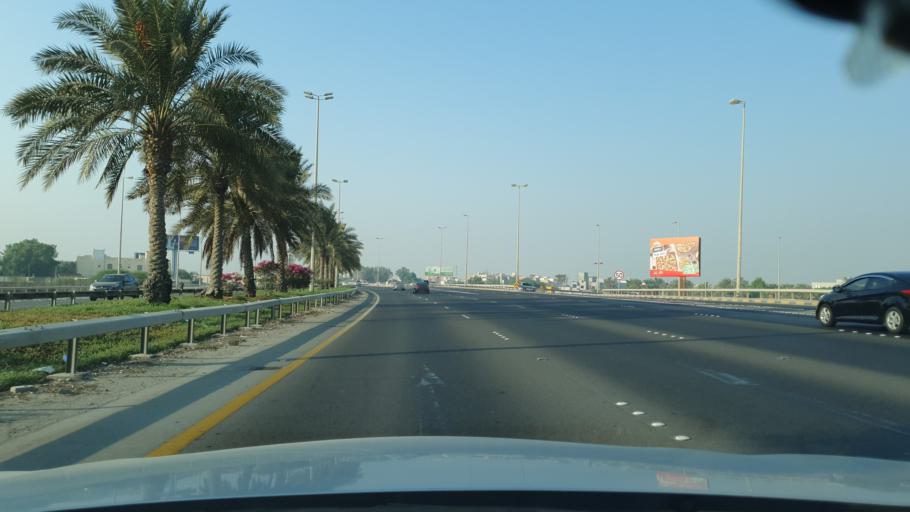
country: BH
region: Manama
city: Jidd Hafs
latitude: 26.2236
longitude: 50.5244
